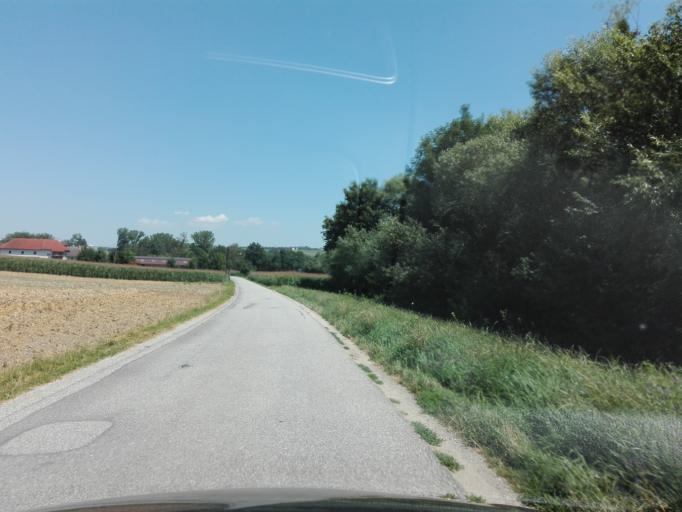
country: AT
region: Upper Austria
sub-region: Politischer Bezirk Urfahr-Umgebung
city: Engerwitzdorf
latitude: 48.2983
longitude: 14.4778
